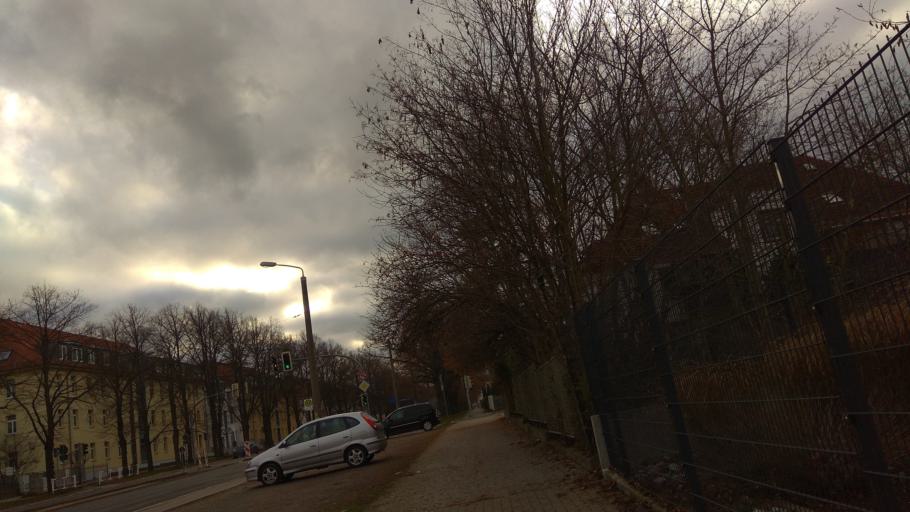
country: DE
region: Saxony-Anhalt
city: Halberstadt
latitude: 51.8785
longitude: 11.0542
